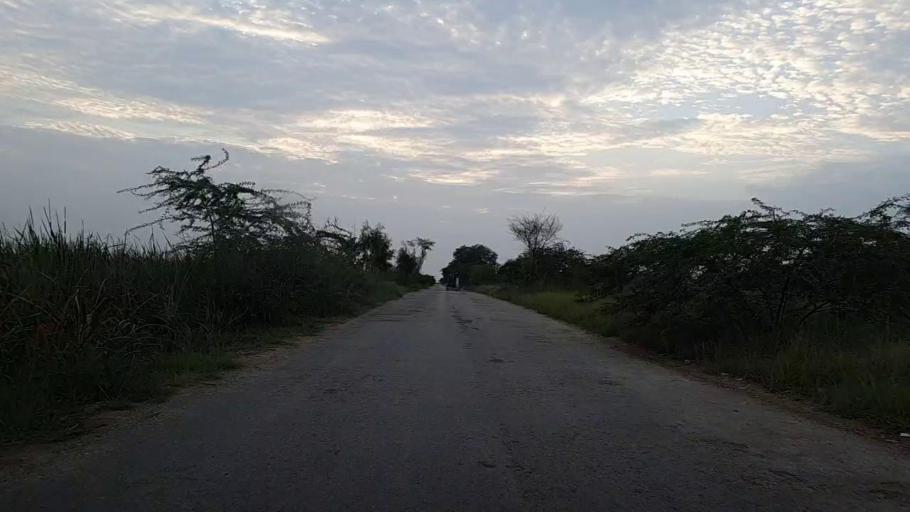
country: PK
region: Sindh
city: Naushahro Firoz
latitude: 26.8174
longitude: 68.1777
